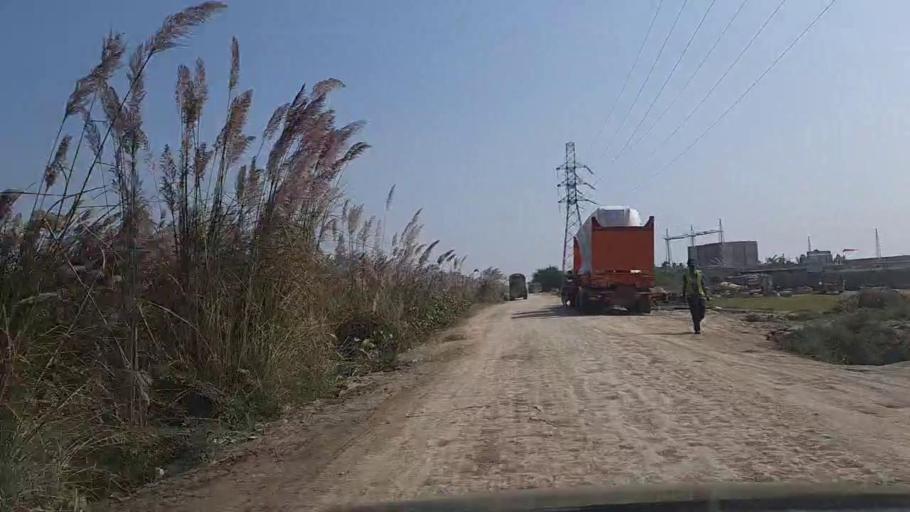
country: PK
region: Sindh
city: Gharo
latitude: 24.7213
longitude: 67.5554
